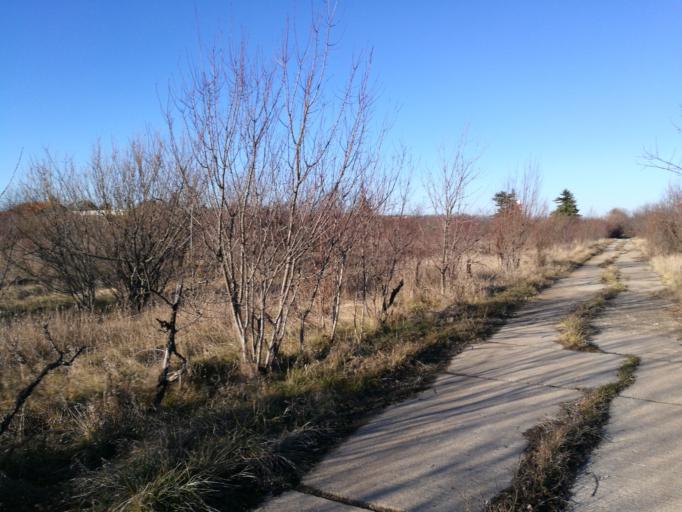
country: RO
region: Ilfov
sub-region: Comuna Otopeni
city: Otopeni
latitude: 44.5051
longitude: 26.0776
